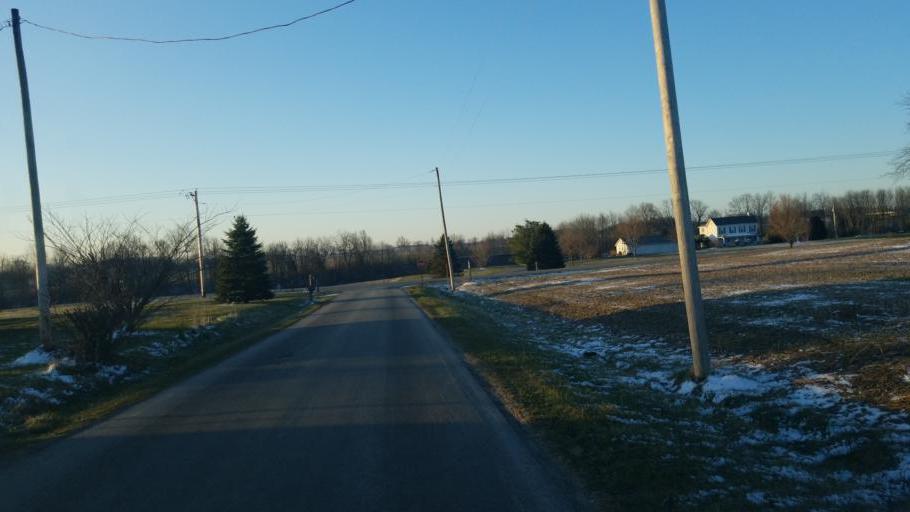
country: US
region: Ohio
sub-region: Highland County
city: Leesburg
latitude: 39.2681
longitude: -83.5030
